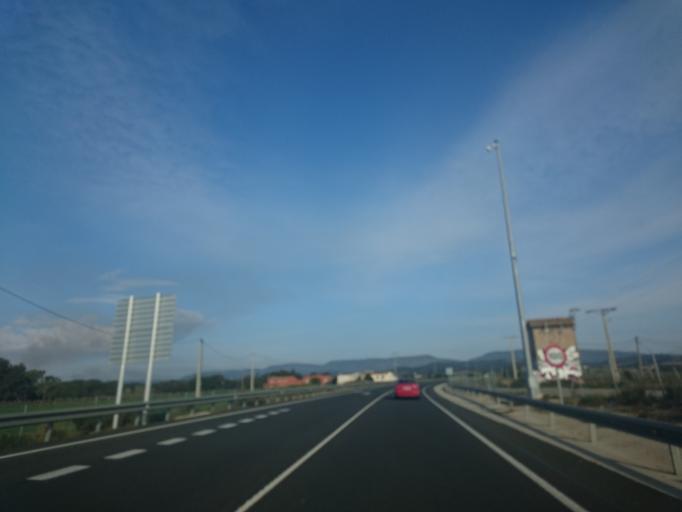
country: ES
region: Catalonia
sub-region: Provincia de Barcelona
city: el Pla del Penedes
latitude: 41.4196
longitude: 1.6900
